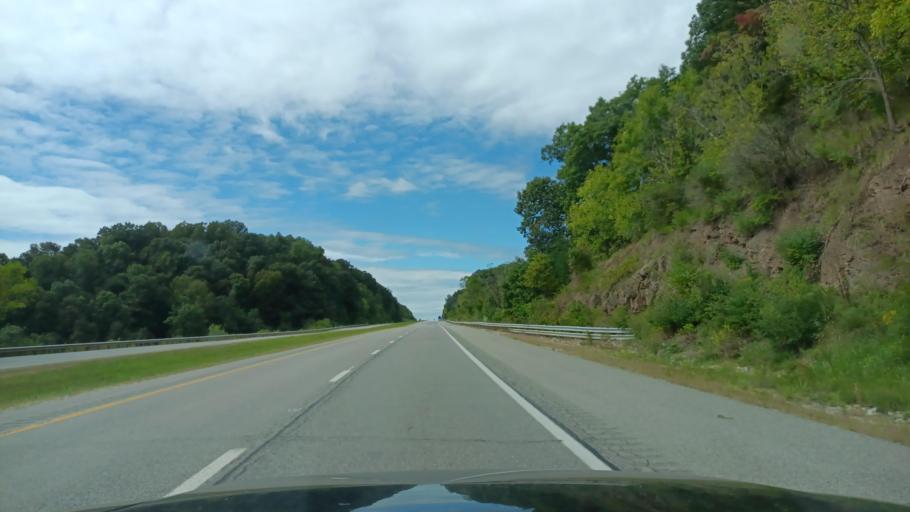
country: US
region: West Virginia
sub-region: Ritchie County
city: Pennsboro
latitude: 39.2650
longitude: -80.9281
